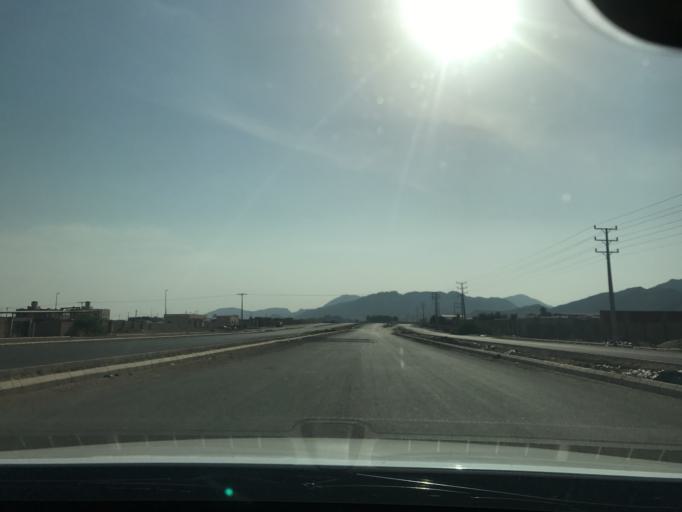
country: SA
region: Makkah
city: Al Jumum
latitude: 21.4540
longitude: 39.5416
